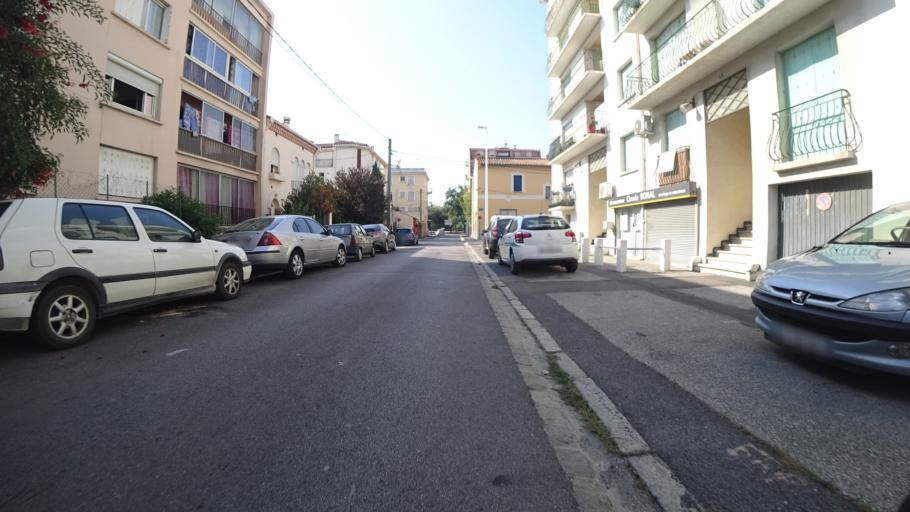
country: FR
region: Languedoc-Roussillon
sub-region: Departement des Pyrenees-Orientales
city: Perpignan
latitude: 42.7032
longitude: 2.8830
